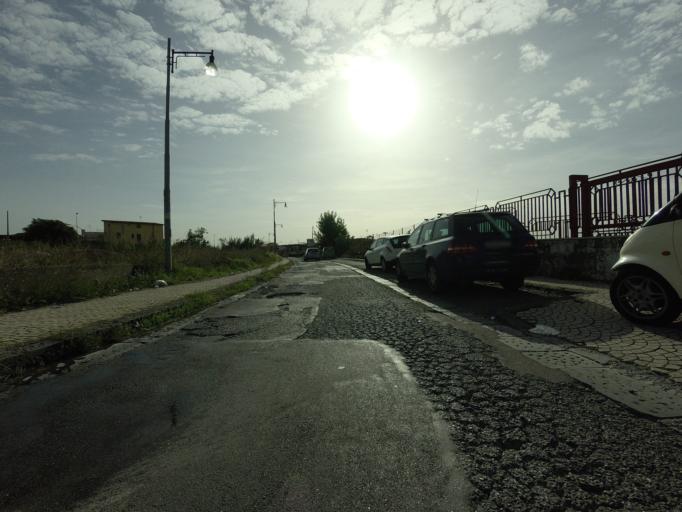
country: IT
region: Campania
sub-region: Provincia di Napoli
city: Ercolano
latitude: 40.8176
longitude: 14.3604
